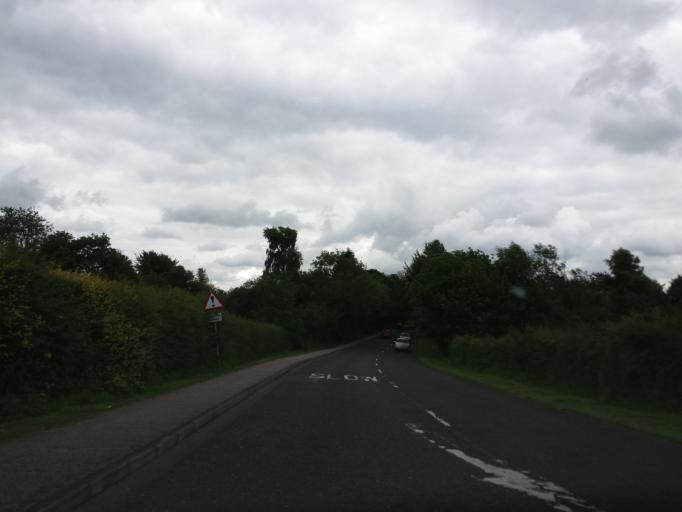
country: GB
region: Scotland
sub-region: Dumfries and Galloway
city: Dumfries
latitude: 55.0651
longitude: -3.6373
